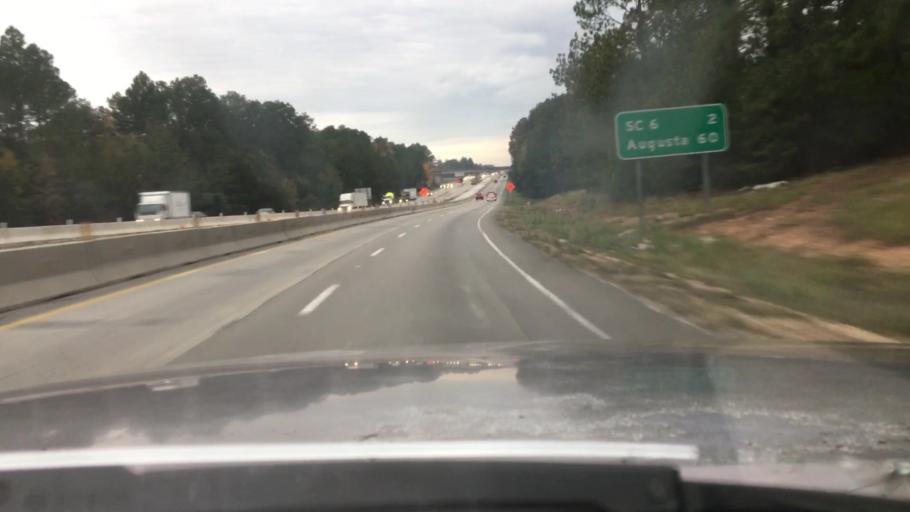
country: US
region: South Carolina
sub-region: Lexington County
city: Lexington
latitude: 33.9686
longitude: -81.2014
